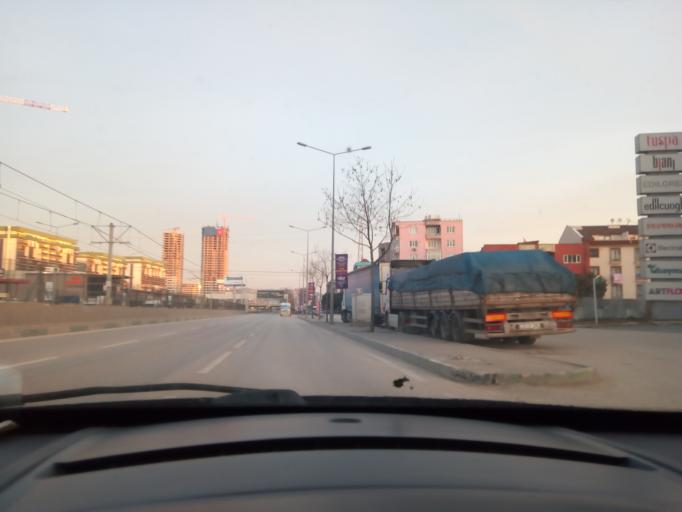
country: TR
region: Bursa
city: Niluefer
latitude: 40.2595
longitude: 28.9517
